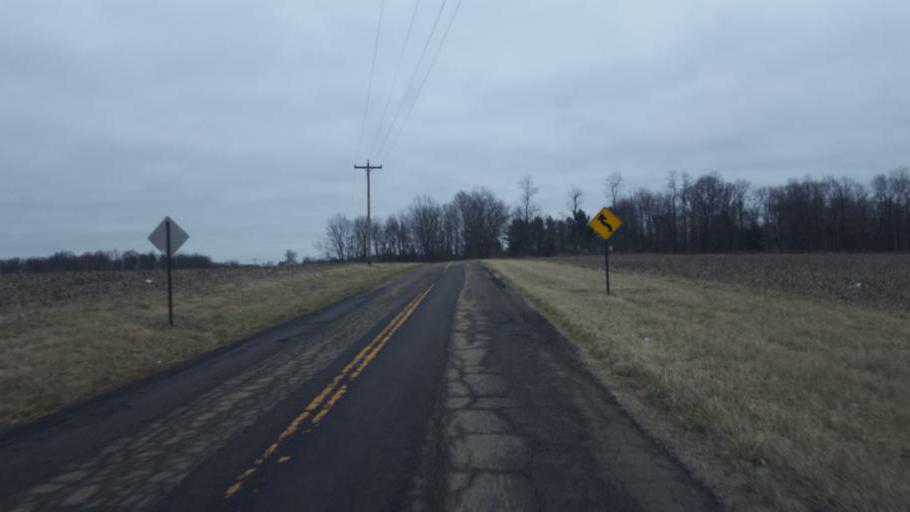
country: US
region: Ohio
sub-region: Knox County
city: Gambier
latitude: 40.4281
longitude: -82.4135
